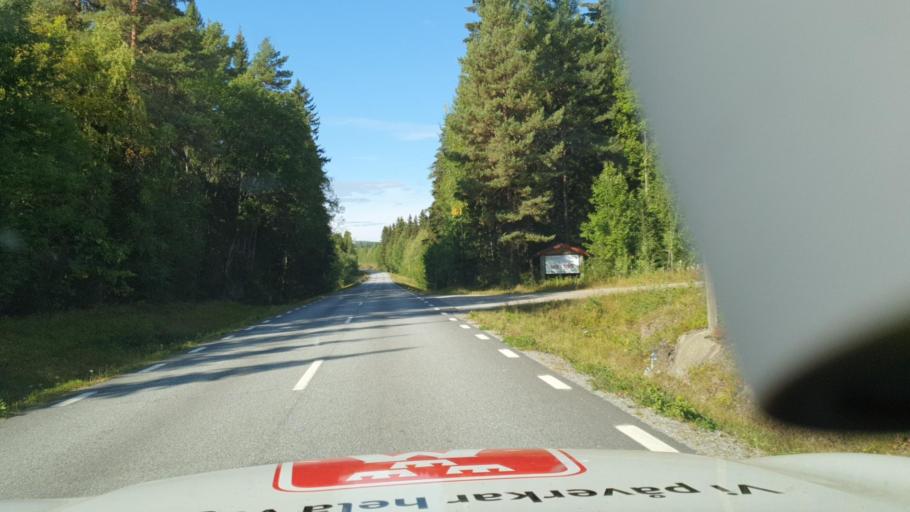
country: SE
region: Vaesterbotten
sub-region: Dorotea Kommun
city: Dorotea
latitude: 64.1073
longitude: 16.2382
